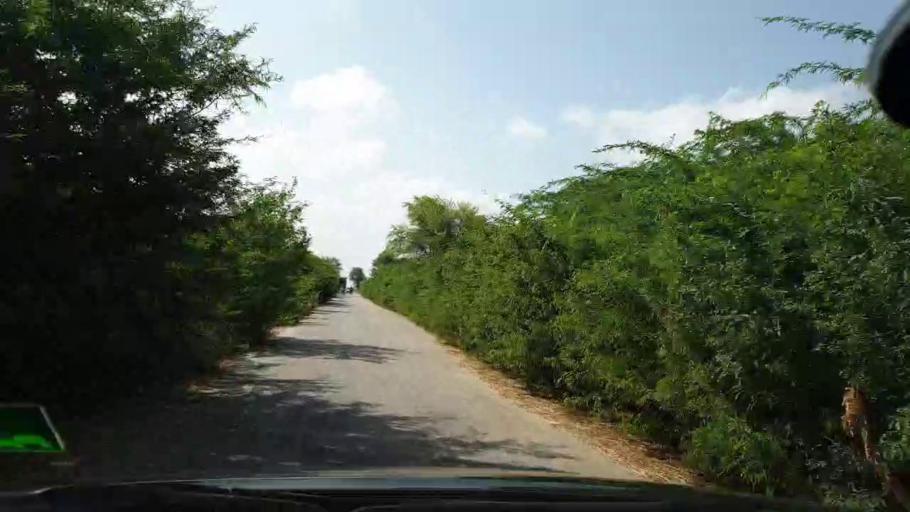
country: PK
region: Sindh
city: Kadhan
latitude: 24.6356
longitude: 69.1158
